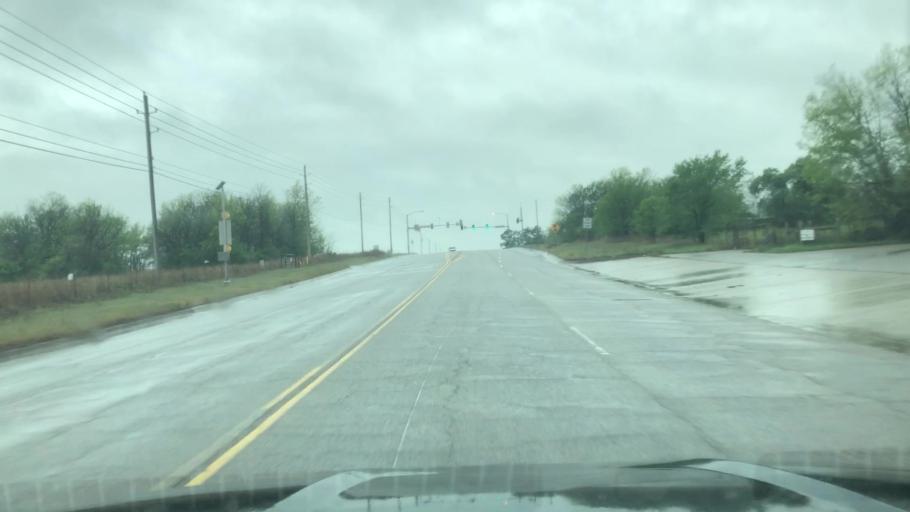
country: US
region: Oklahoma
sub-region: Tulsa County
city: Owasso
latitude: 36.2641
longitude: -95.8887
